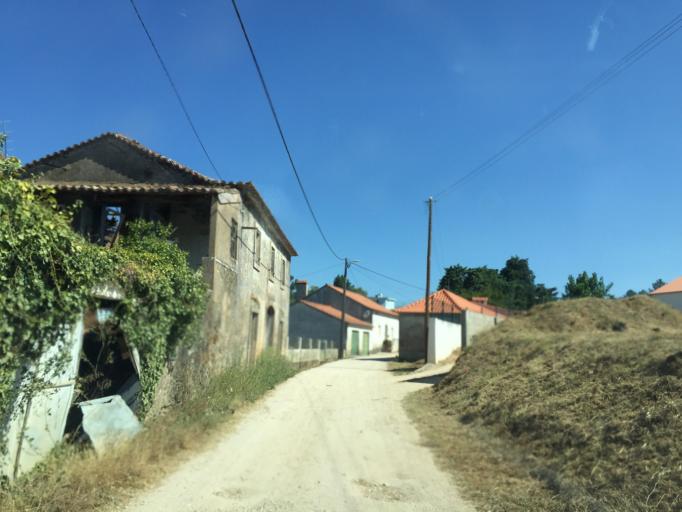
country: PT
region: Santarem
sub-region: Tomar
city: Tomar
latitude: 39.6049
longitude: -8.3488
